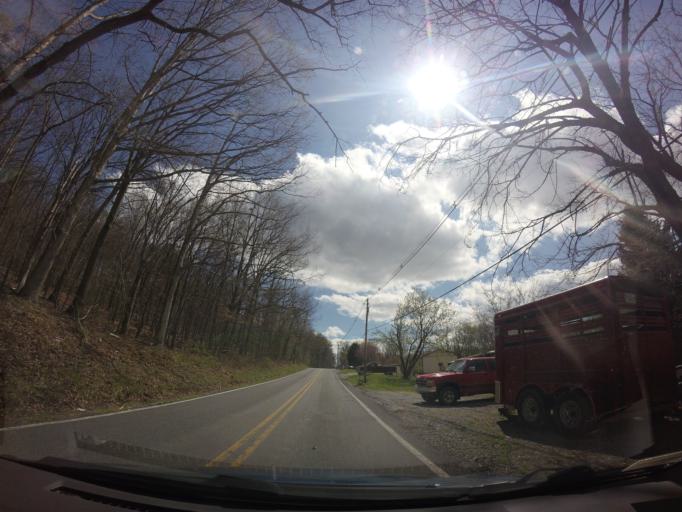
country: US
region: Maryland
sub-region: Washington County
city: Keedysville
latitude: 39.4498
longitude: -77.7023
